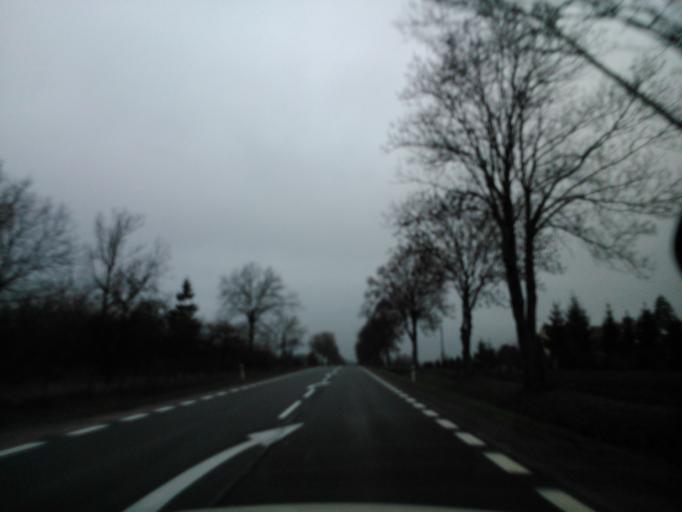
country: PL
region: Swietokrzyskie
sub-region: Powiat opatowski
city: Wojciechowice
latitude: 50.8265
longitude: 21.5995
